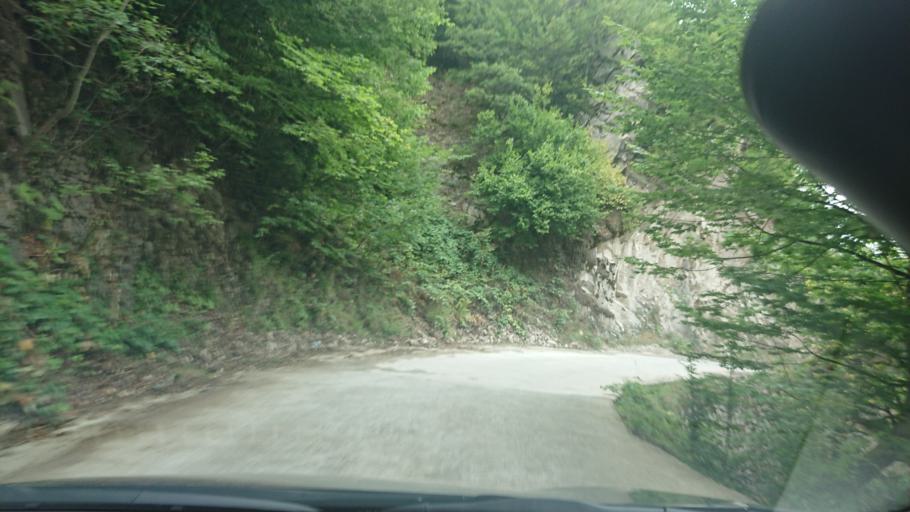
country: TR
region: Gumushane
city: Kurtun
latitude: 40.6811
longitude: 39.0495
